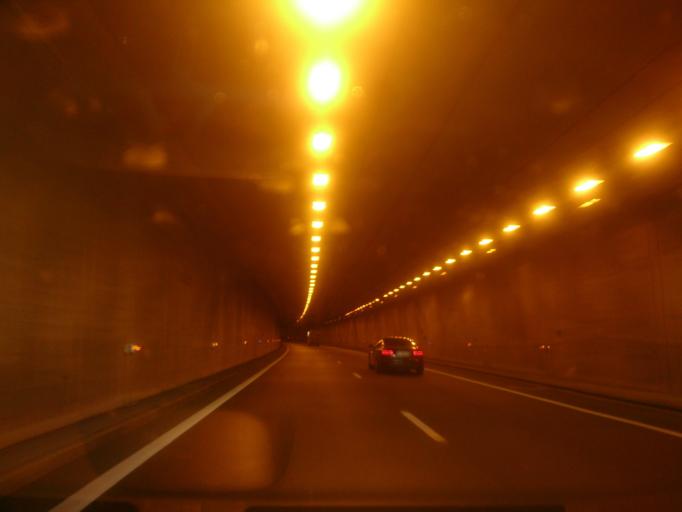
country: FR
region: Midi-Pyrenees
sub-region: Departement du Lot
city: Souillac
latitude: 44.8590
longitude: 1.5013
